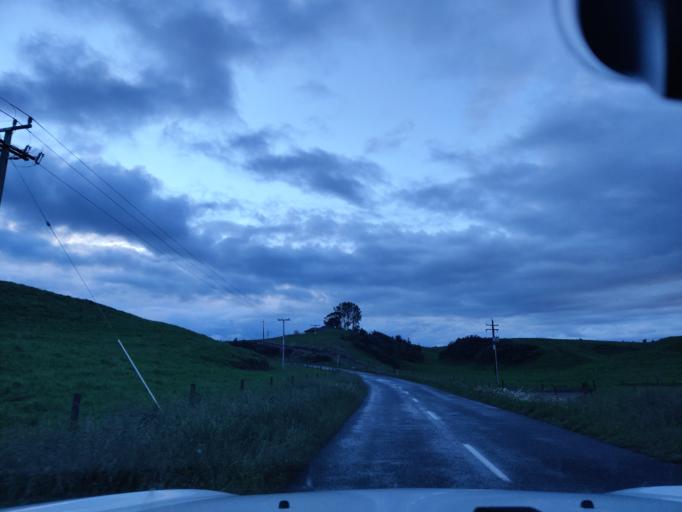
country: NZ
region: Waikato
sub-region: South Waikato District
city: Tokoroa
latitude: -38.1808
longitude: 175.7822
